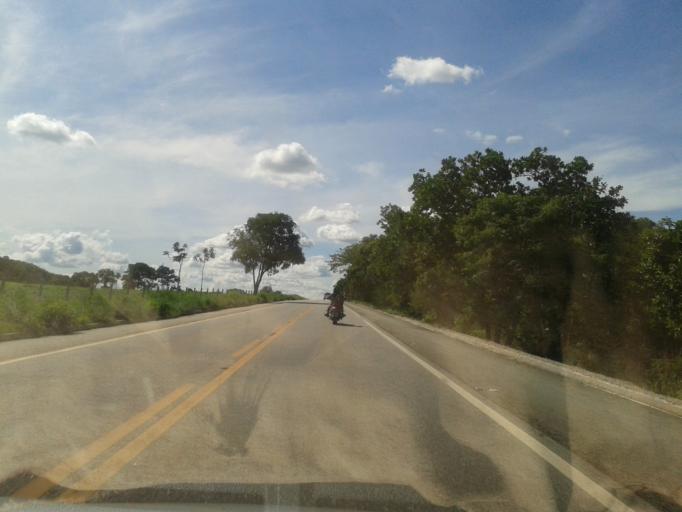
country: BR
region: Goias
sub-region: Itapirapua
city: Itapirapua
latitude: -15.3000
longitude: -50.4531
